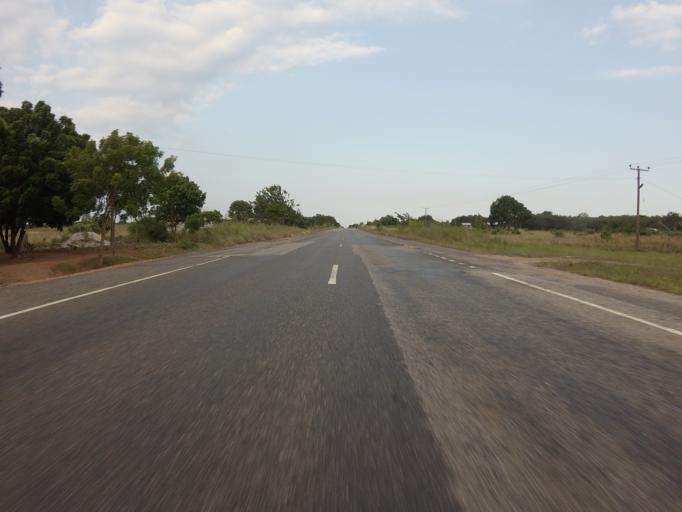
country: GH
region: Volta
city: Anloga
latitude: 6.0879
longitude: 0.5413
